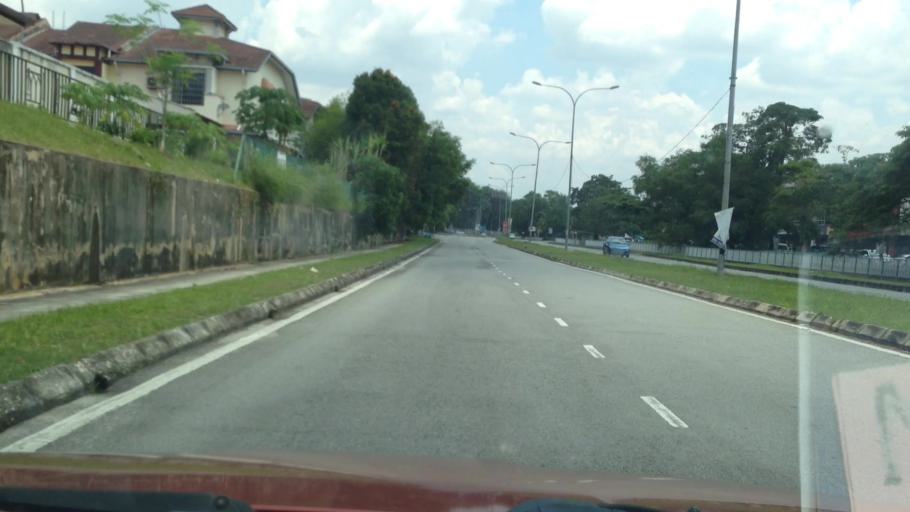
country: MY
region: Selangor
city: Kampung Baru Subang
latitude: 3.1657
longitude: 101.5473
